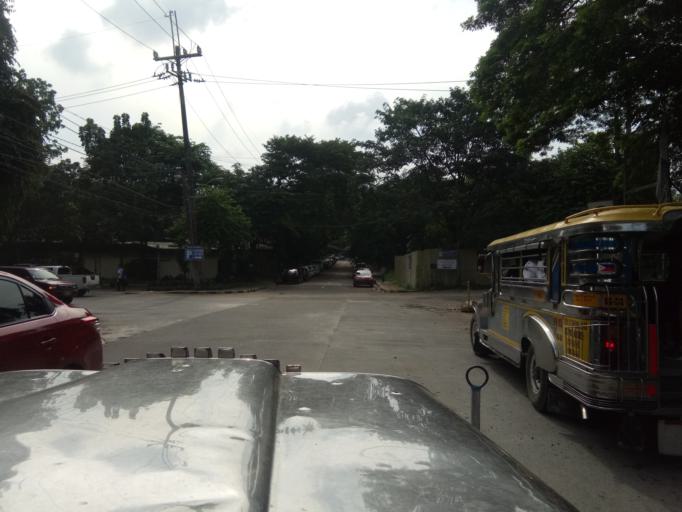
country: PH
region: Metro Manila
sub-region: Quezon City
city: Quezon City
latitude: 14.6577
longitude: 121.0631
